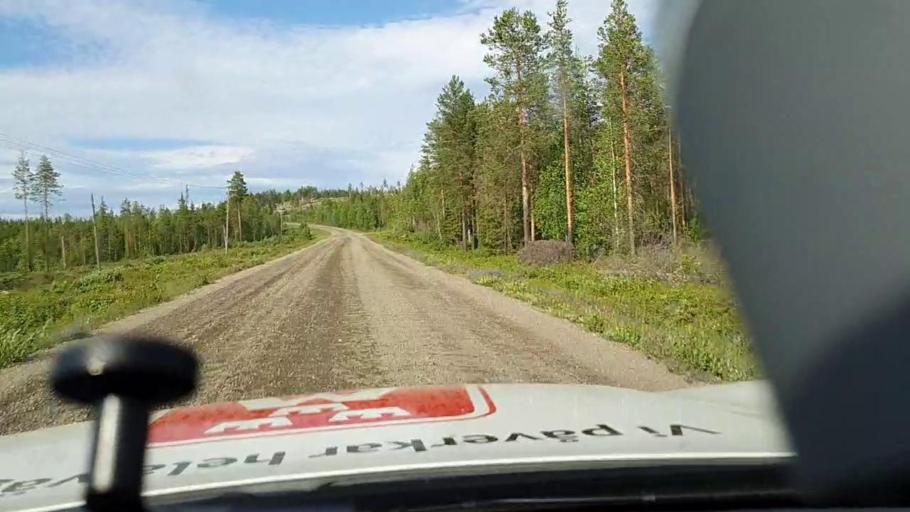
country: SE
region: Norrbotten
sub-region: Alvsbyns Kommun
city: AElvsbyn
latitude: 66.1632
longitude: 21.0522
